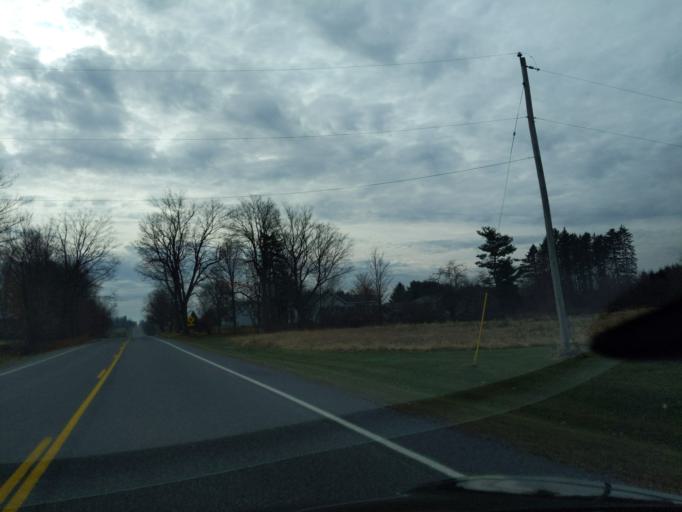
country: US
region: Michigan
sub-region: Ingham County
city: Mason
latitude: 42.5410
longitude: -84.5225
